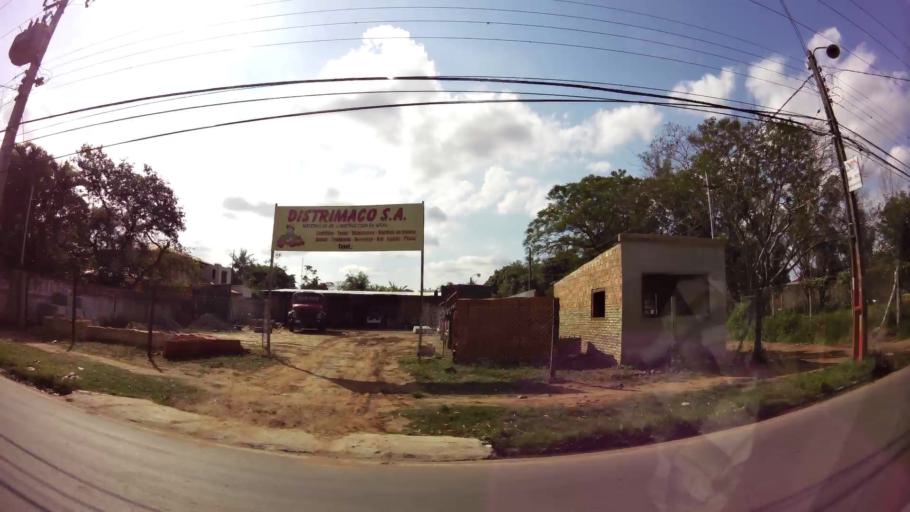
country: PY
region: Central
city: Fernando de la Mora
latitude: -25.3225
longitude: -57.5401
